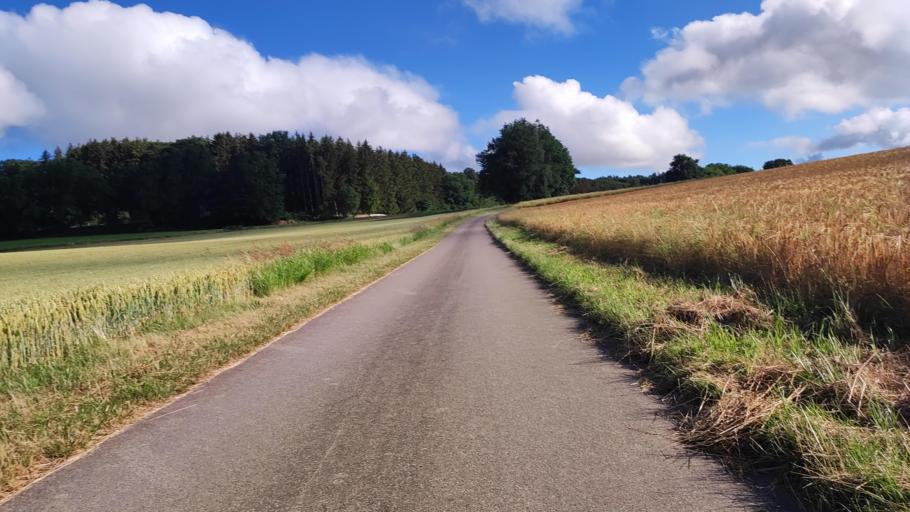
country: DE
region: Bavaria
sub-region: Swabia
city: Zusmarshausen
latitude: 48.3826
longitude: 10.5895
